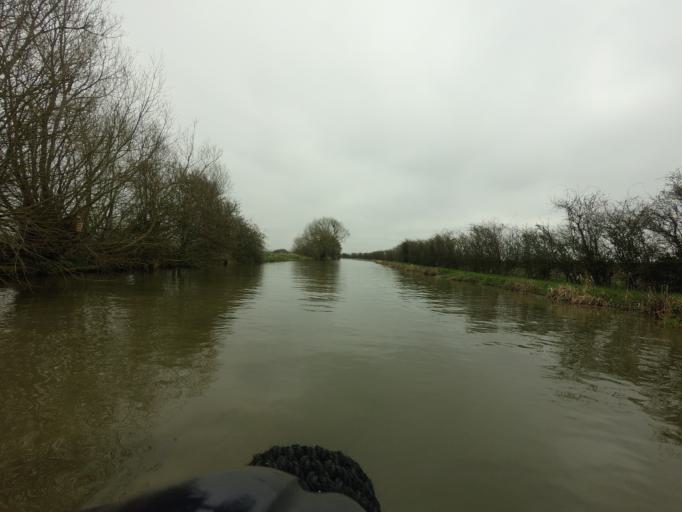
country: GB
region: England
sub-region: Central Bedfordshire
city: Leighton Buzzard
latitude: 51.8868
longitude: -0.6593
